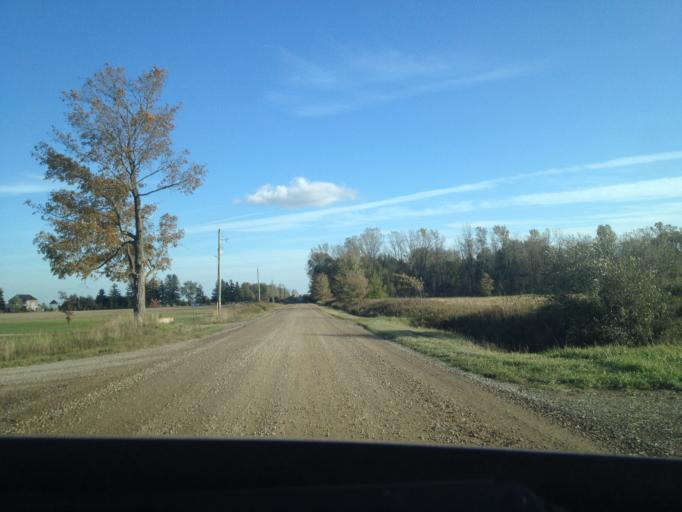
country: CA
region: Ontario
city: Delaware
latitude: 42.6579
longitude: -81.5555
